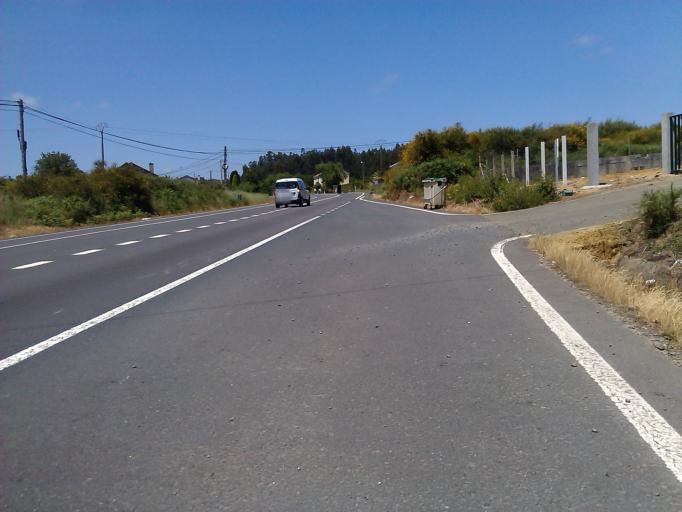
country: ES
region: Galicia
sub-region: Provincia da Coruna
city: Oroso
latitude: 42.9082
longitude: -8.3974
